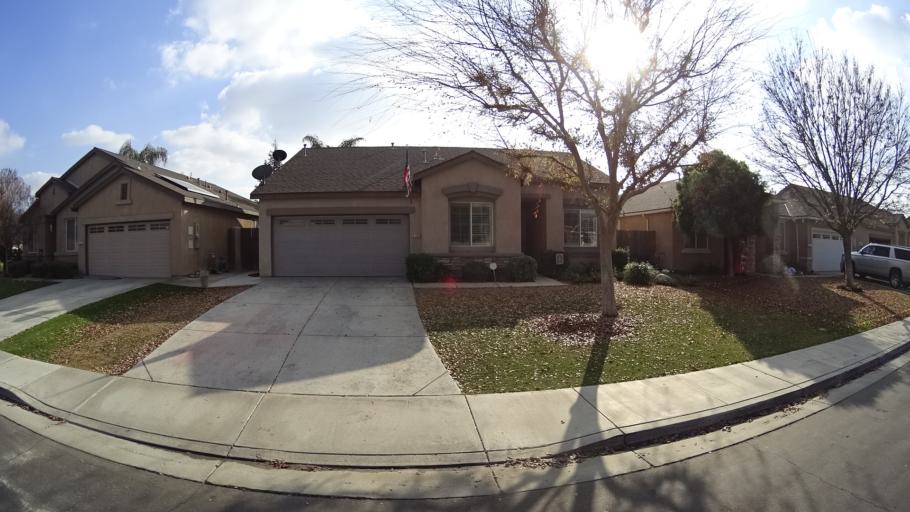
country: US
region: California
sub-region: Kern County
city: Greenacres
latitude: 35.3055
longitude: -119.1038
